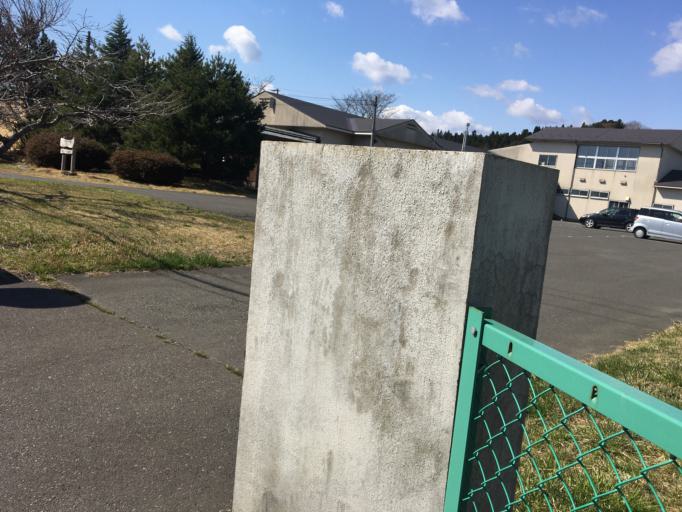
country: JP
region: Aomori
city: Hachinohe
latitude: 40.2074
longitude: 141.7937
